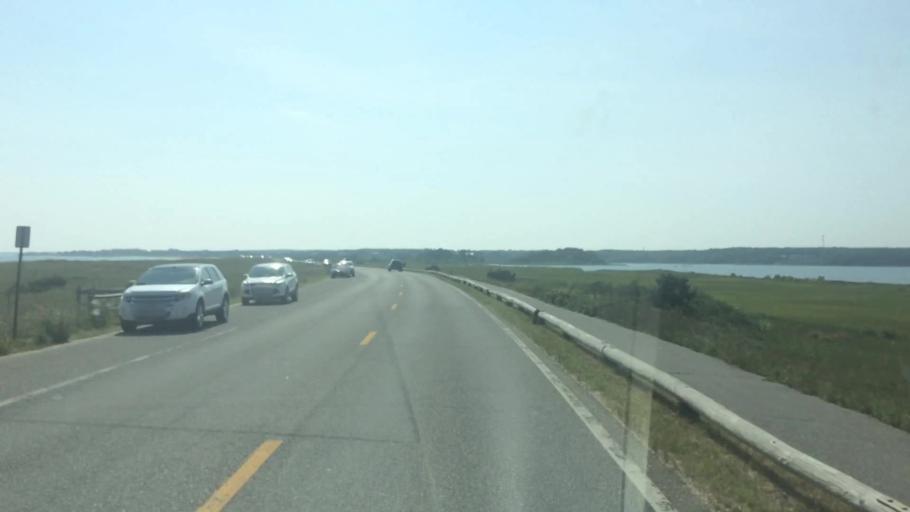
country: US
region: Massachusetts
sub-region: Dukes County
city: Edgartown
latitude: 41.4133
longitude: -70.5458
